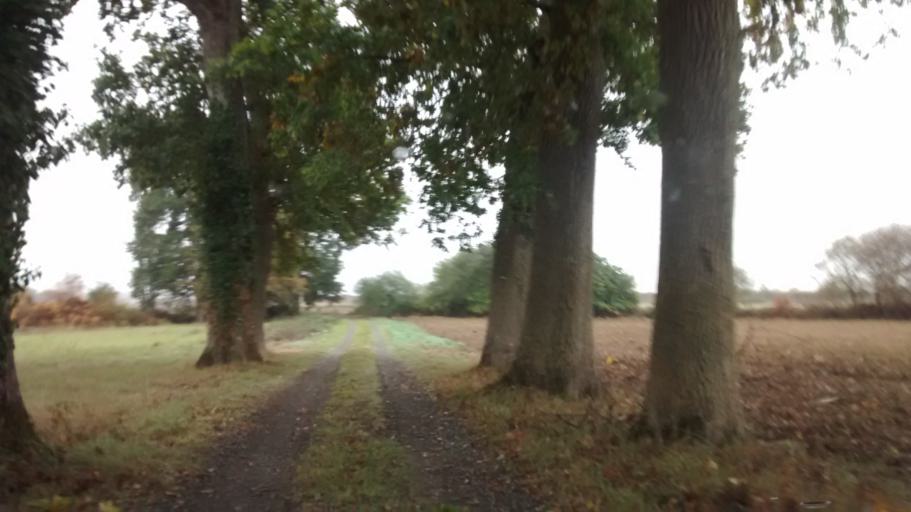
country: FR
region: Brittany
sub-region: Departement d'Ille-et-Vilaine
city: Betton
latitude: 48.1523
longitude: -1.6208
